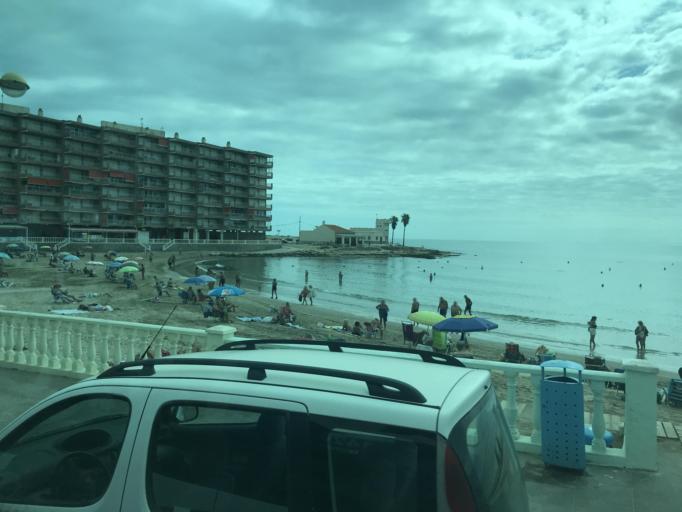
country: ES
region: Valencia
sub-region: Provincia de Alicante
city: Torrevieja
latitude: 37.9841
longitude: -0.6593
